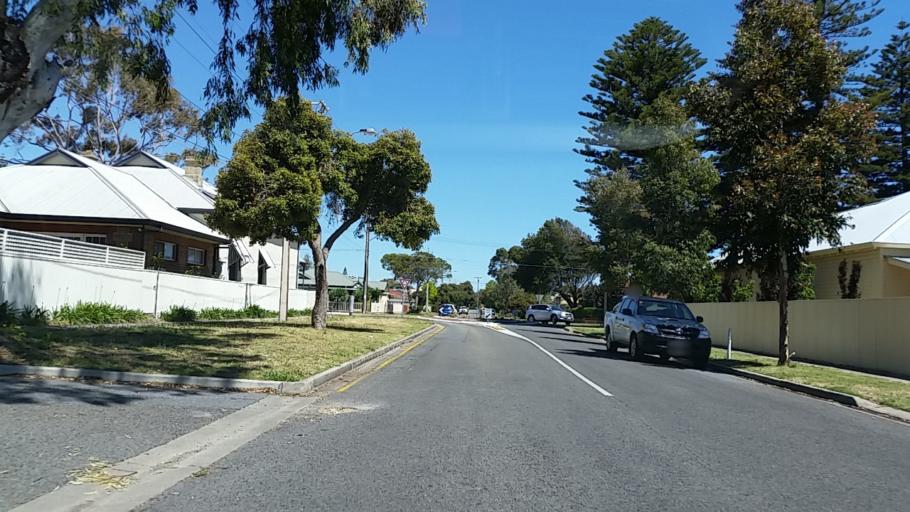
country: AU
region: South Australia
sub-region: Charles Sturt
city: Grange
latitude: -34.9017
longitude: 138.4949
